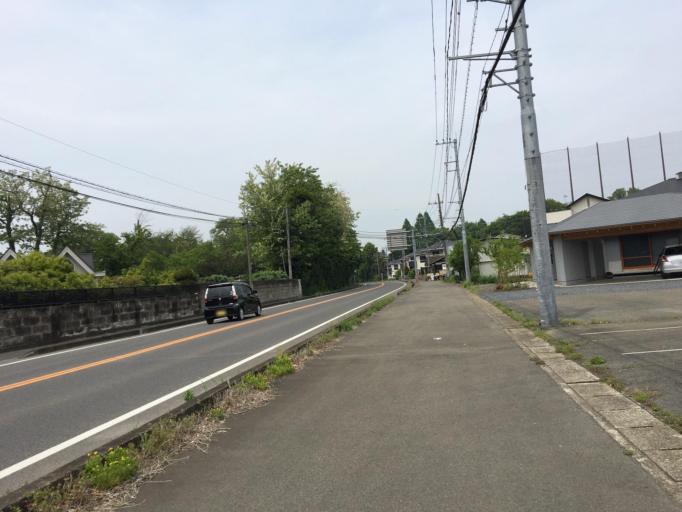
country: JP
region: Tochigi
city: Oyama
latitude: 36.3402
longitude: 139.8171
